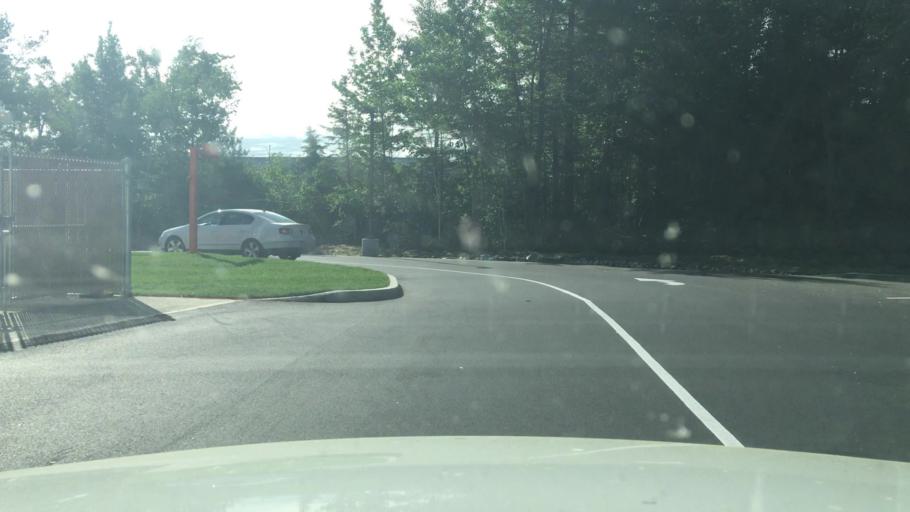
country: US
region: Maine
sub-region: Cumberland County
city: South Portland Gardens
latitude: 43.6147
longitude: -70.3110
